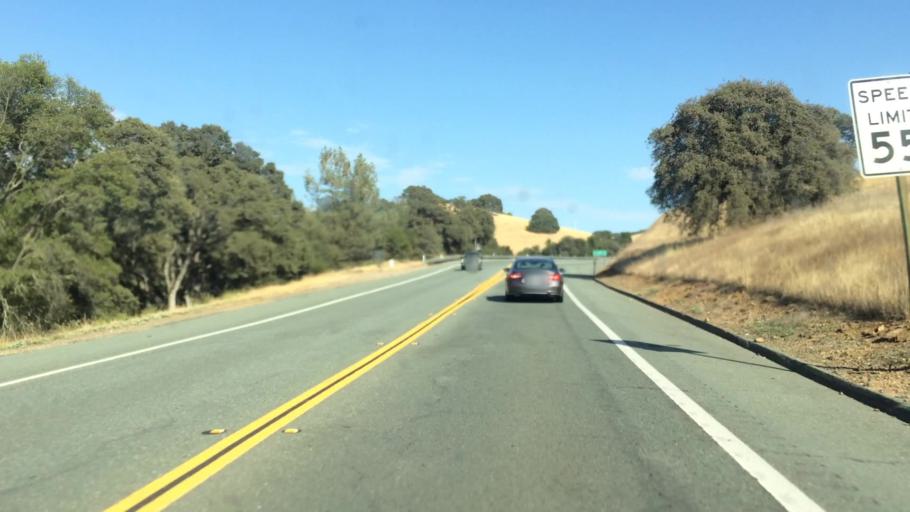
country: US
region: California
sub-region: Amador County
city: Sutter Creek
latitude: 38.4223
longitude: -120.8441
